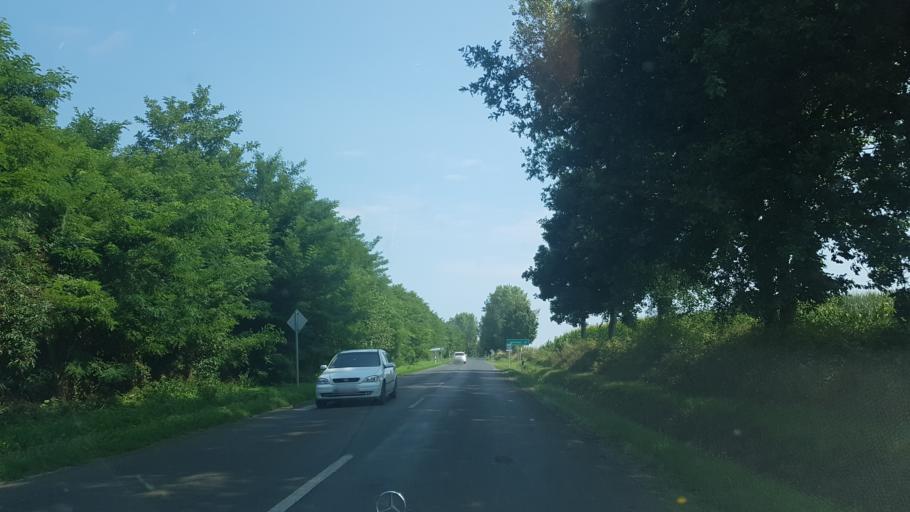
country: HU
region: Somogy
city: Bohonye
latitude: 46.3873
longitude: 17.3738
